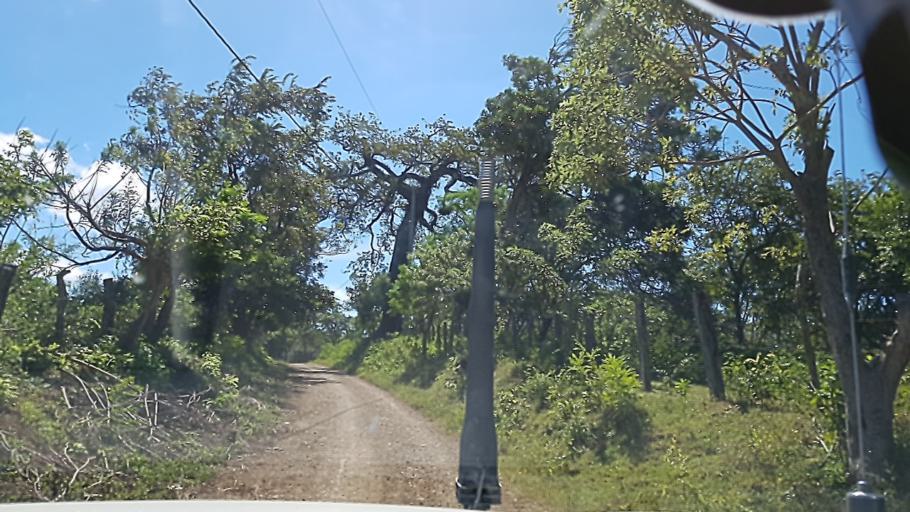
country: NI
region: Carazo
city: Santa Teresa
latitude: 11.7182
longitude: -86.1725
